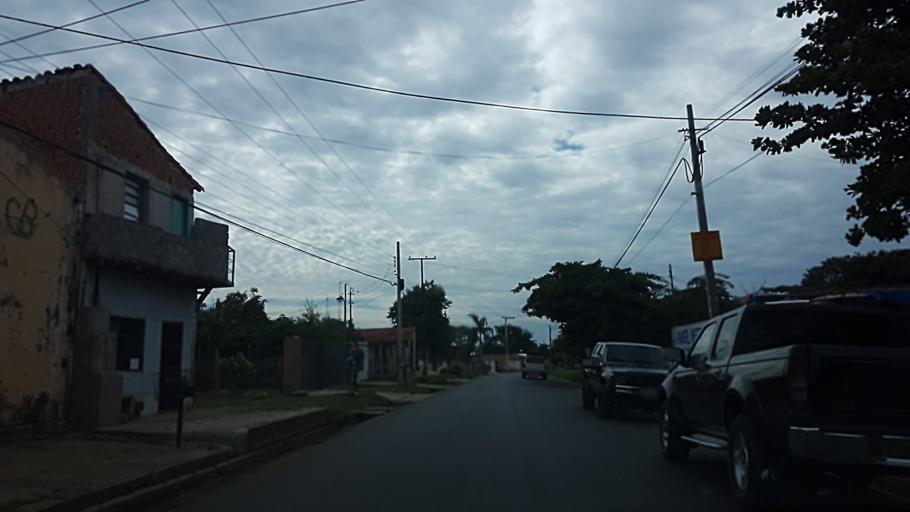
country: PY
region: Central
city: Colonia Mariano Roque Alonso
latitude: -25.2198
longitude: -57.5272
